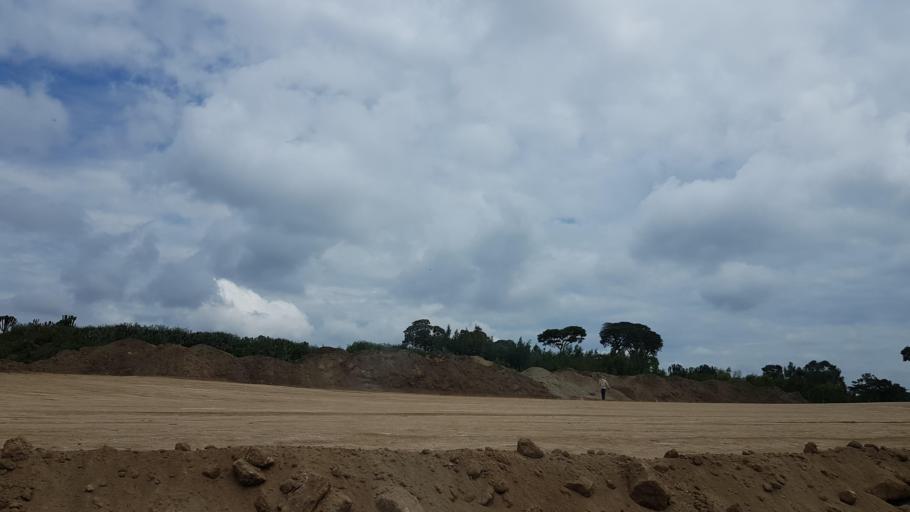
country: ET
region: Oromiya
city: Shashemene
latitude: 7.2486
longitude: 38.5896
